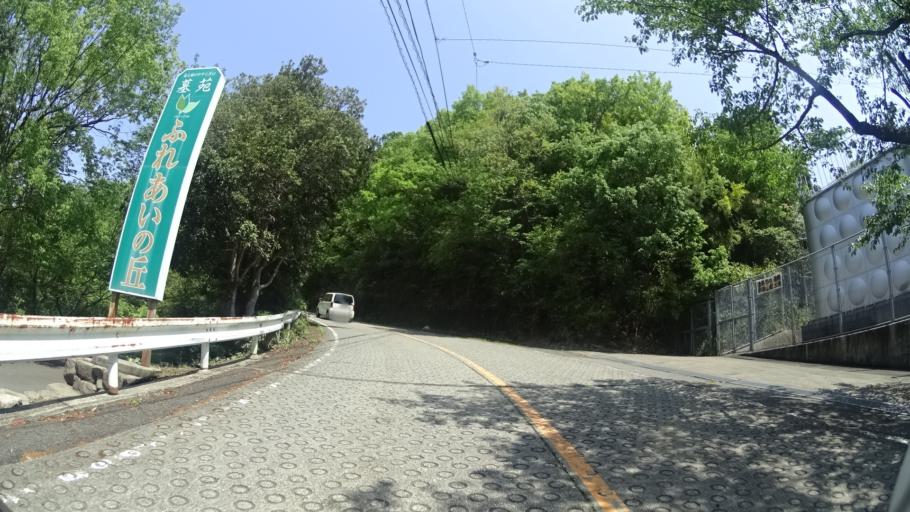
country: JP
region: Tokushima
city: Tokushima-shi
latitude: 34.0605
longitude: 134.5417
